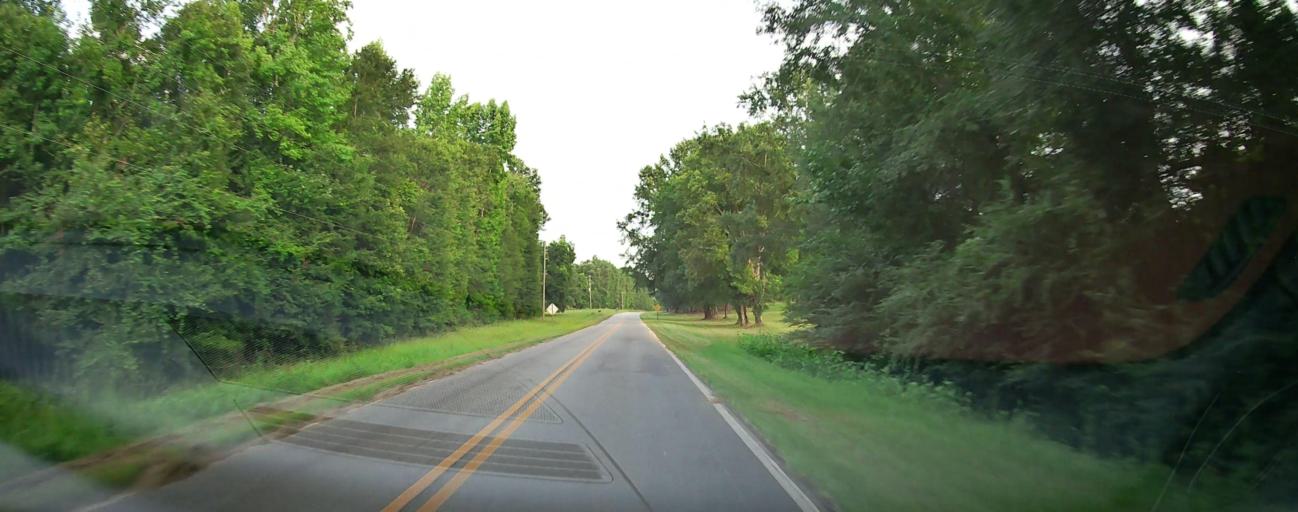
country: US
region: Georgia
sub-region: Crawford County
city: Roberta
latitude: 32.6666
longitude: -84.0673
